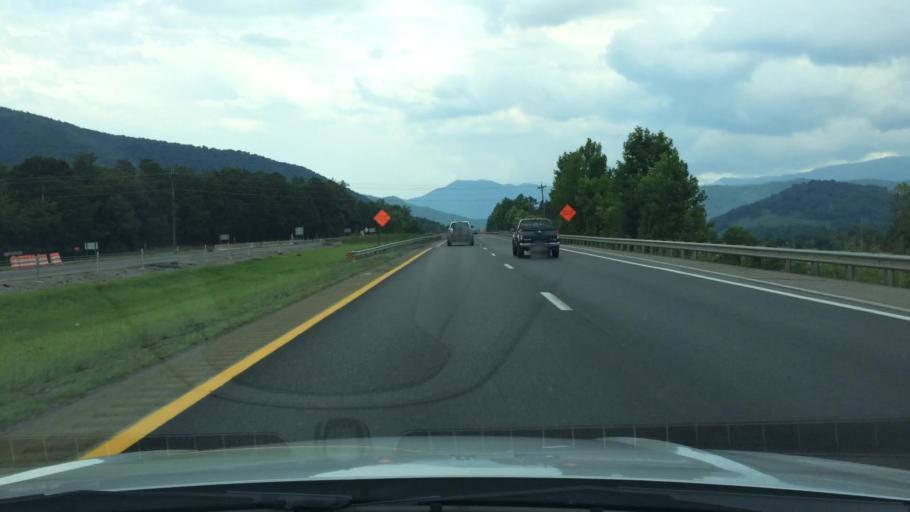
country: US
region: Tennessee
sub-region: Cocke County
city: Newport
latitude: 35.8803
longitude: -83.1870
